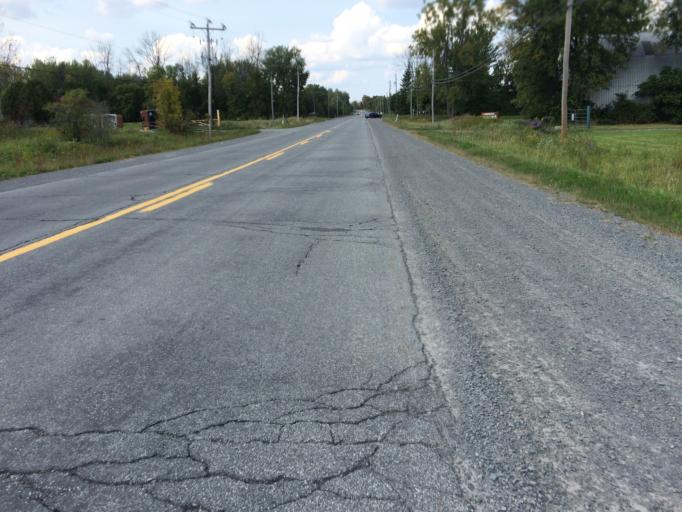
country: CA
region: Ontario
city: Bells Corners
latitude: 45.1998
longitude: -75.6465
